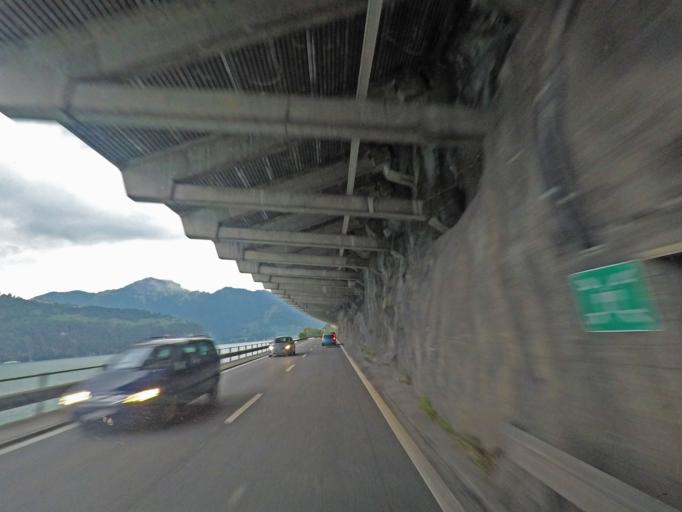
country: CH
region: Schwyz
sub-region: Bezirk Schwyz
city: Ingenbohl
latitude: 46.9619
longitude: 8.6164
